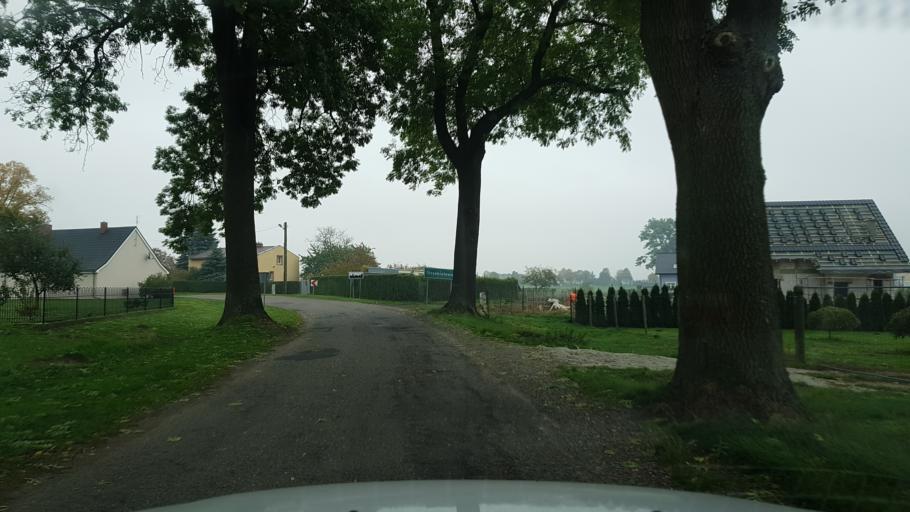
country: PL
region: West Pomeranian Voivodeship
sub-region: Powiat pyrzycki
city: Warnice
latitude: 53.2553
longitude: 15.0801
